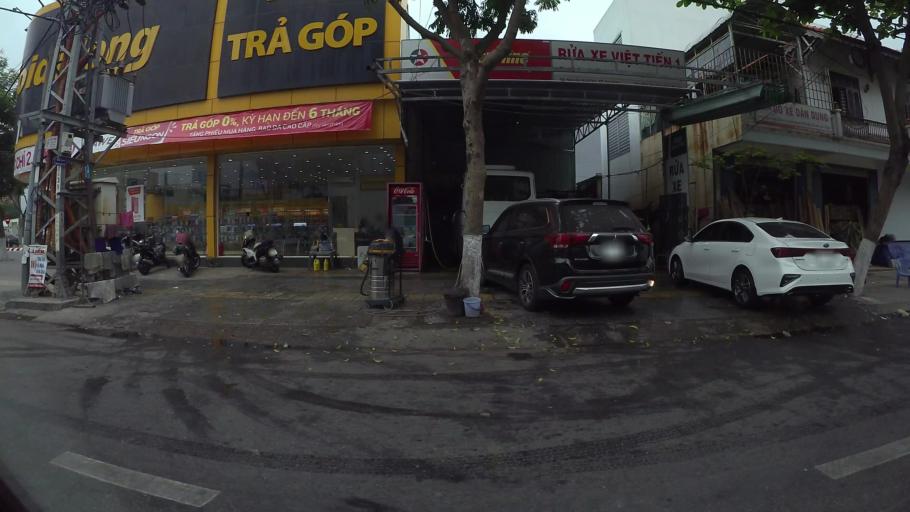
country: VN
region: Da Nang
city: Cam Le
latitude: 16.0369
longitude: 108.2104
